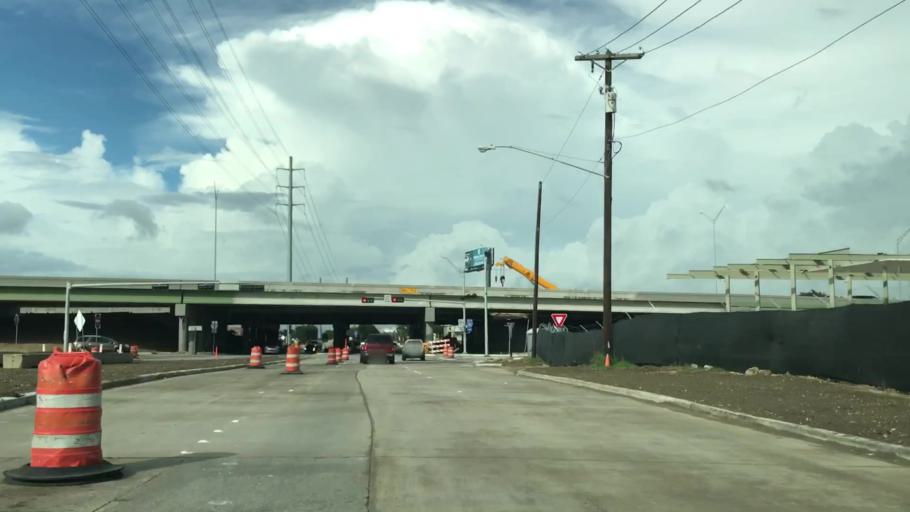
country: US
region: Texas
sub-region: Dallas County
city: Irving
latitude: 32.8266
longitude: -96.8869
